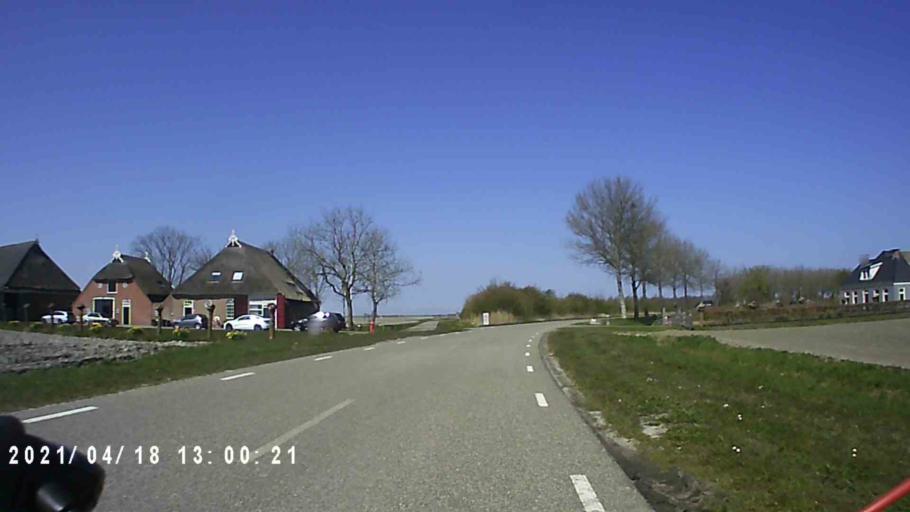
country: NL
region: Friesland
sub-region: Gemeente Dongeradeel
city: Anjum
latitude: 53.3975
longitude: 6.0875
